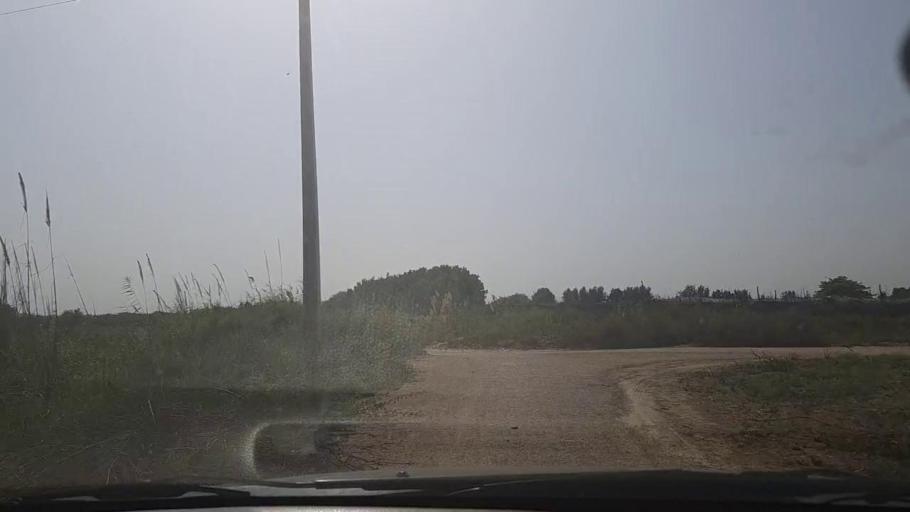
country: PK
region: Sindh
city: Keti Bandar
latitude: 24.1969
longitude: 67.5450
